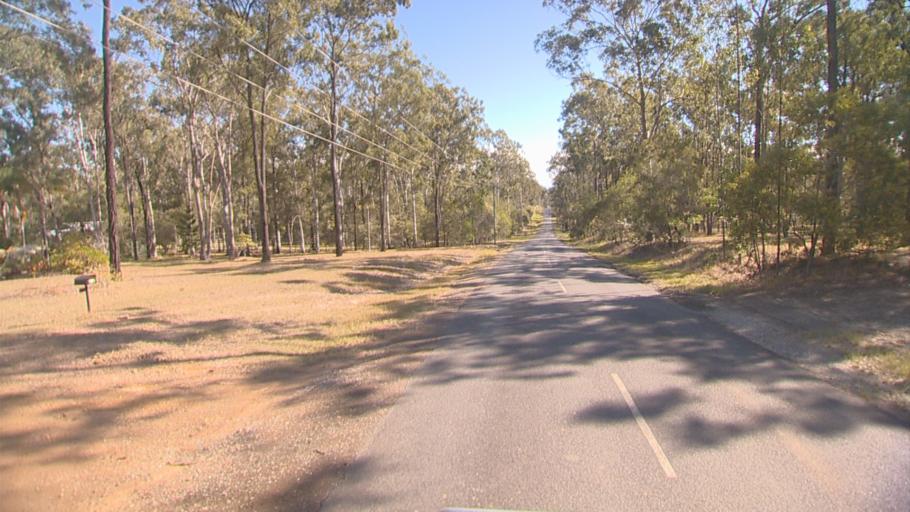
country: AU
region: Queensland
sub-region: Logan
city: Chambers Flat
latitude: -27.8165
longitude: 153.0680
